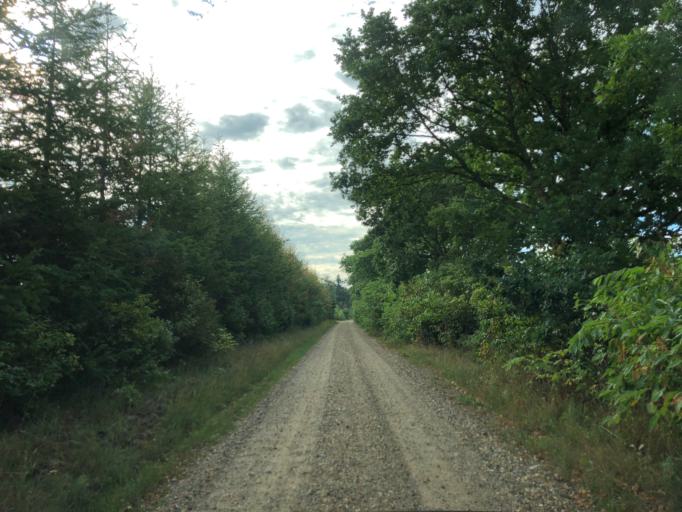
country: DK
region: Central Jutland
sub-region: Holstebro Kommune
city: Ulfborg
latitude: 56.1856
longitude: 8.3446
